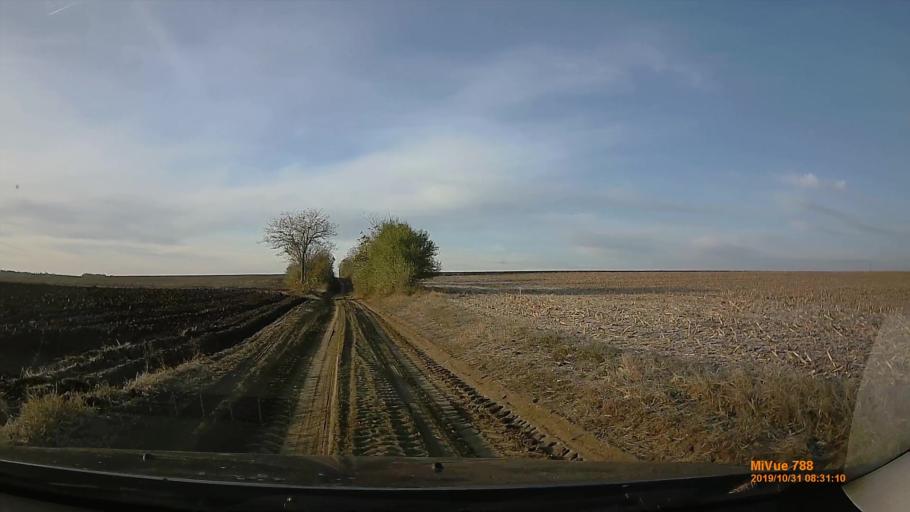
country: HU
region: Pest
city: Tapiobicske
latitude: 47.3487
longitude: 19.6668
